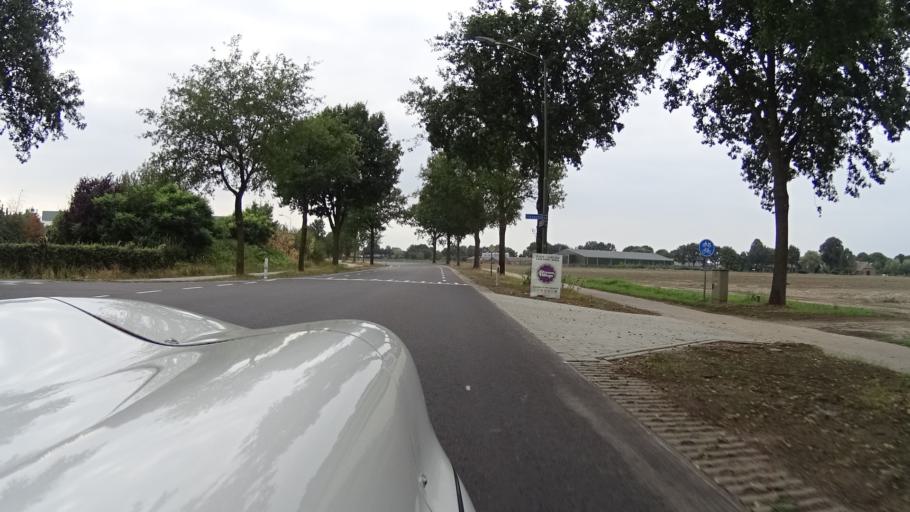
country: NL
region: North Brabant
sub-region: Gemeente Veghel
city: Erp
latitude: 51.5921
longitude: 5.6232
